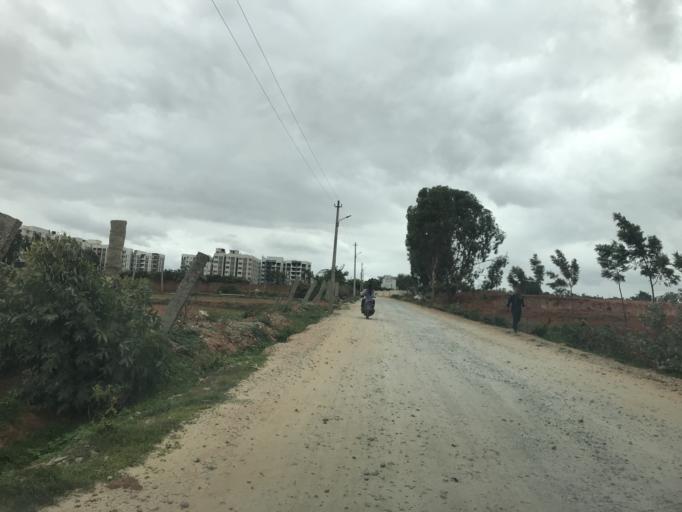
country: IN
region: Karnataka
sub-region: Bangalore Rural
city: Devanhalli
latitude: 13.2141
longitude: 77.6574
